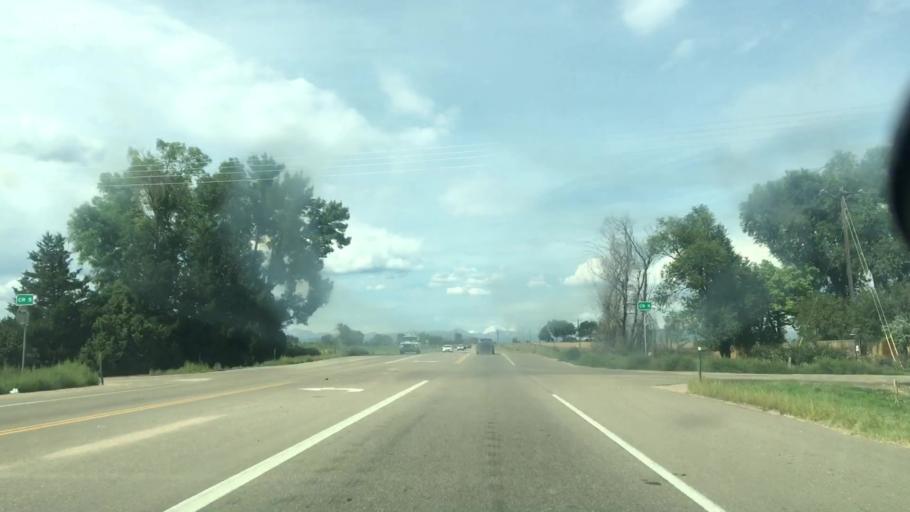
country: US
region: Colorado
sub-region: Weld County
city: Mead
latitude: 40.2040
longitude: -105.0170
